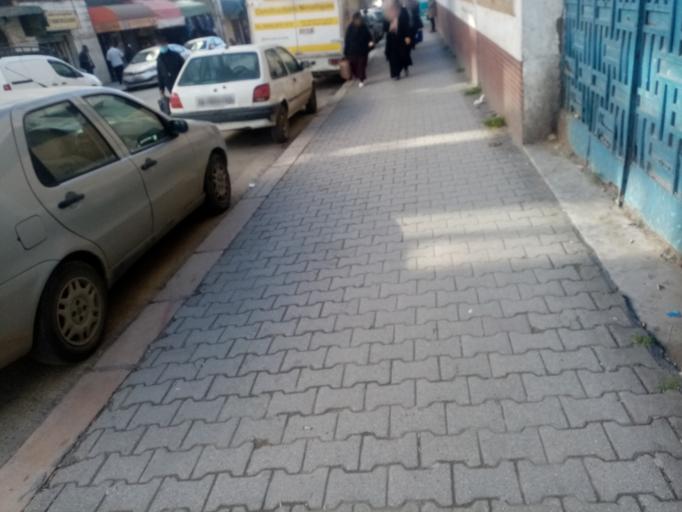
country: TN
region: Tunis
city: Tunis
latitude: 36.7920
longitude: 10.1741
